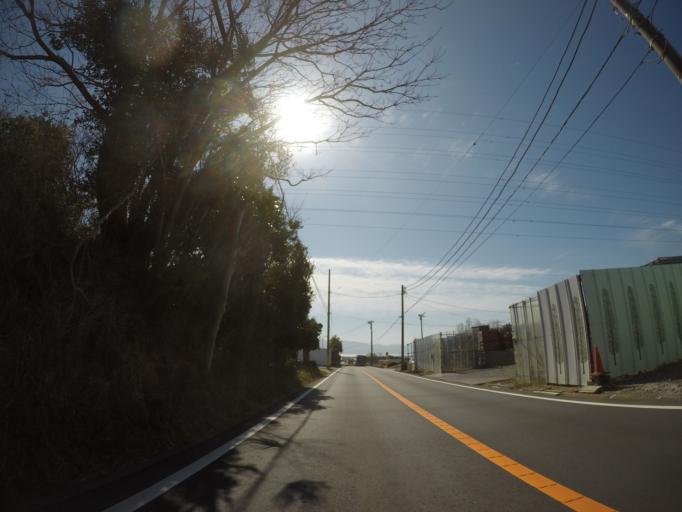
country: JP
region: Shizuoka
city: Numazu
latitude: 35.1352
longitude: 138.8360
